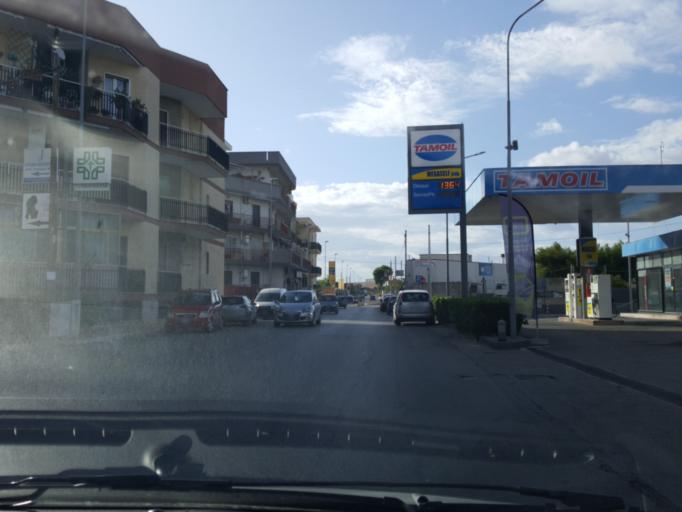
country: IT
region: Apulia
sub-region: Provincia di Bari
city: Triggiano
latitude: 41.0656
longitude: 16.9333
